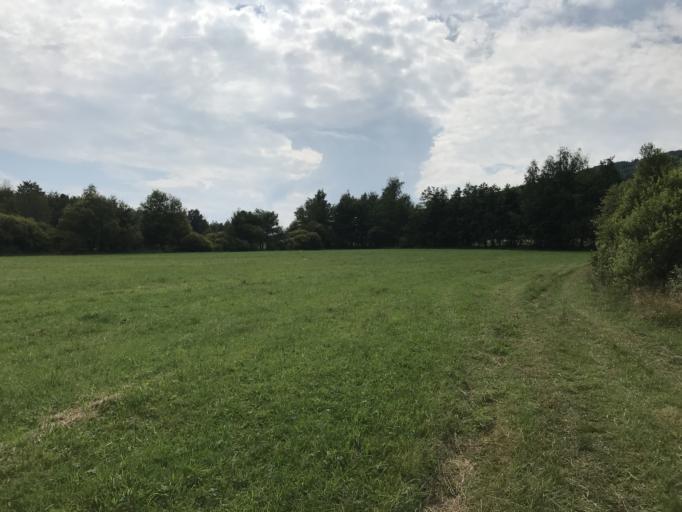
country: PL
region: Lesser Poland Voivodeship
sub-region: Powiat gorlicki
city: Uscie Gorlickie
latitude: 49.4574
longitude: 21.2279
